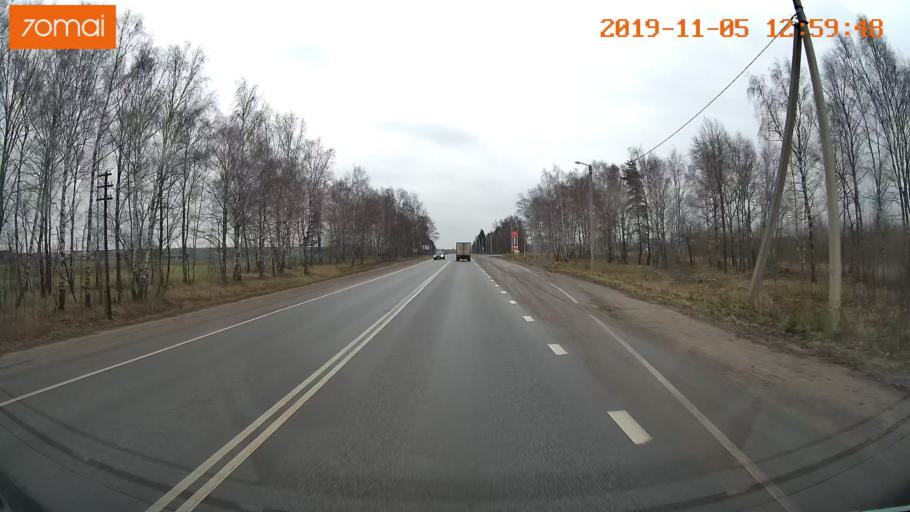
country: RU
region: Ivanovo
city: Kokhma
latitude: 56.9167
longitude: 41.1353
